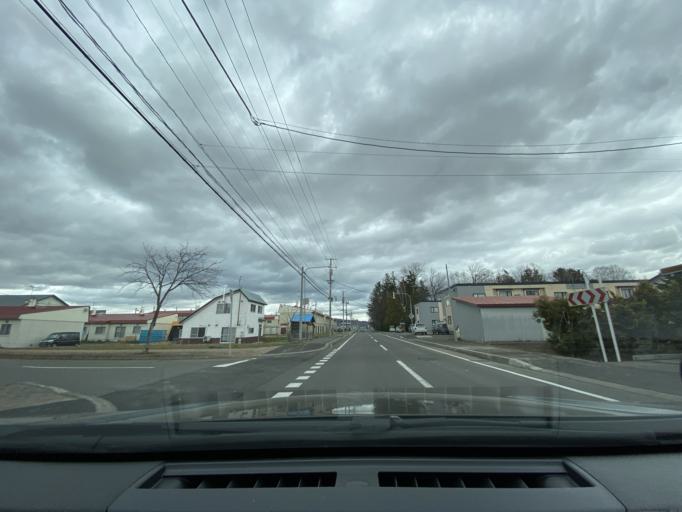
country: JP
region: Hokkaido
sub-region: Asahikawa-shi
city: Asahikawa
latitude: 43.8711
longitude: 142.4792
